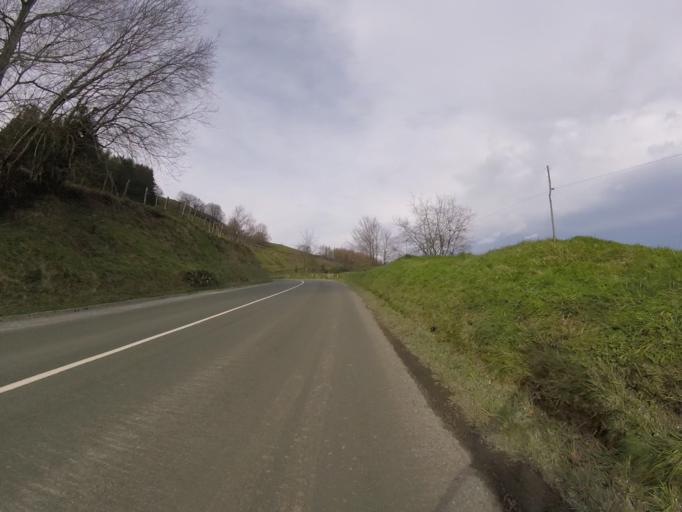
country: ES
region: Basque Country
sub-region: Provincia de Guipuzcoa
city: Errezil
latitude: 43.1485
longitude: -2.1847
